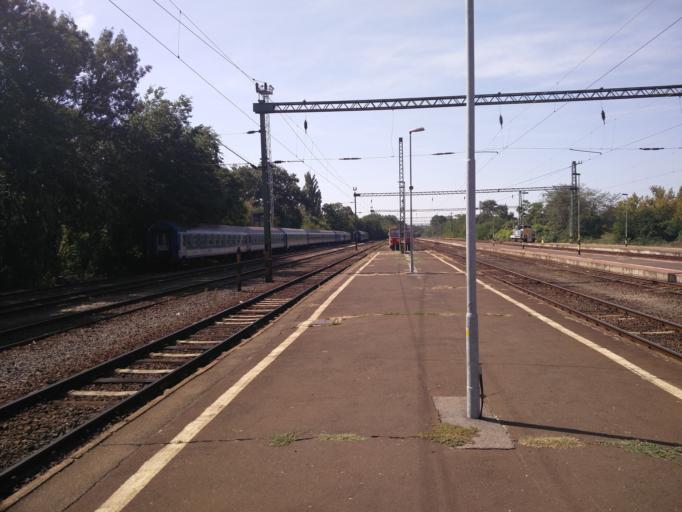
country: HU
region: Csongrad
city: Szeged
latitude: 46.2378
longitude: 20.1424
